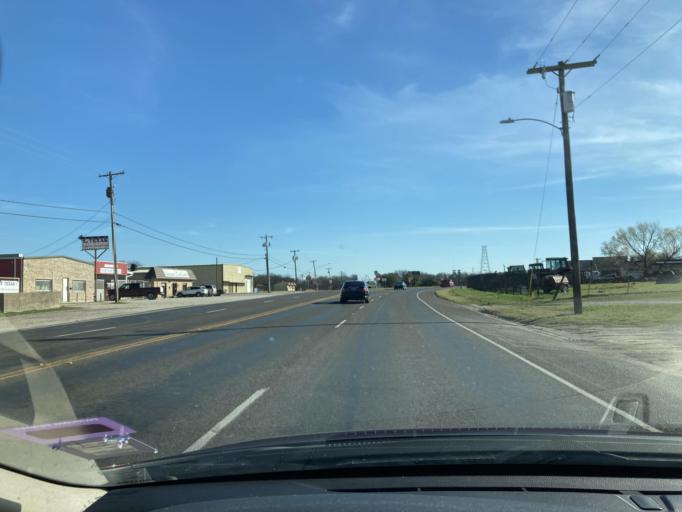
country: US
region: Texas
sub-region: Navarro County
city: Corsicana
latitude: 32.0859
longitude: -96.4538
